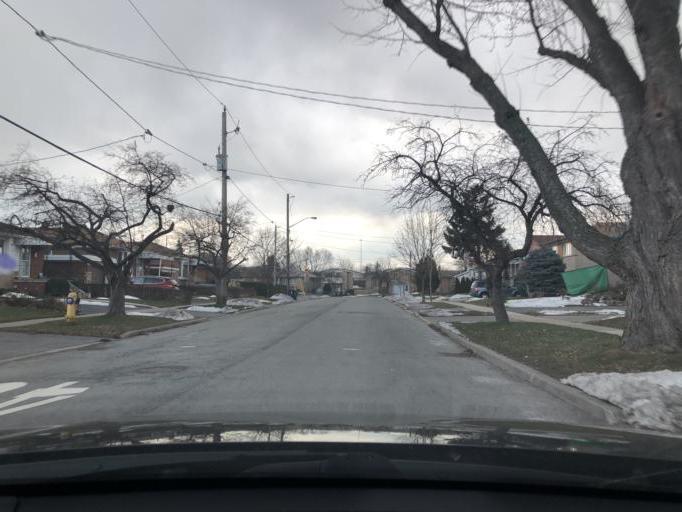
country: CA
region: Ontario
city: Scarborough
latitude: 43.7781
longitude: -79.2936
